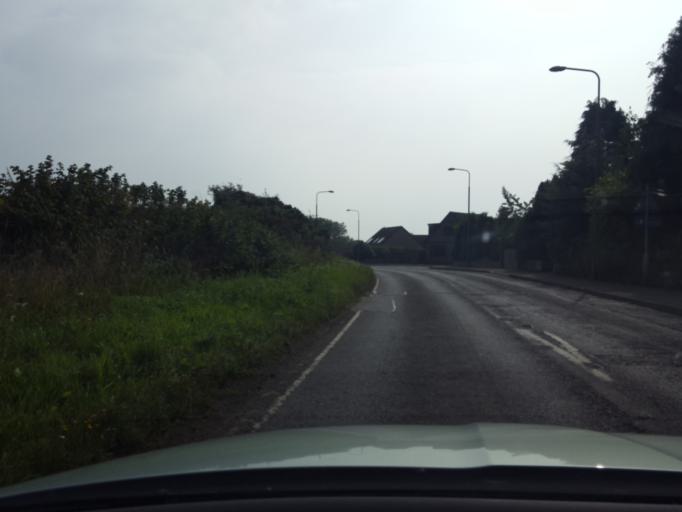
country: GB
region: Scotland
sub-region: Fife
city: Crossgates
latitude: 56.0813
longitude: -3.3762
